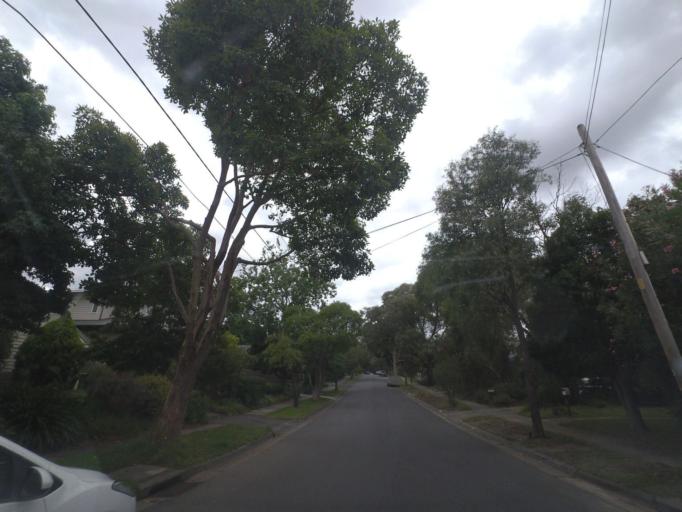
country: AU
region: Victoria
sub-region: Whitehorse
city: Blackburn
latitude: -37.8265
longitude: 145.1562
